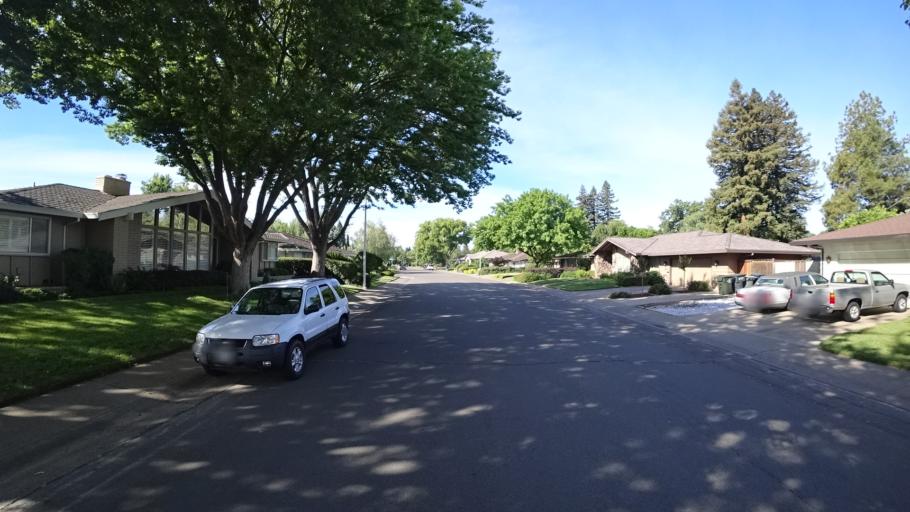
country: US
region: California
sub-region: Sacramento County
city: Rosemont
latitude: 38.5672
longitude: -121.4008
